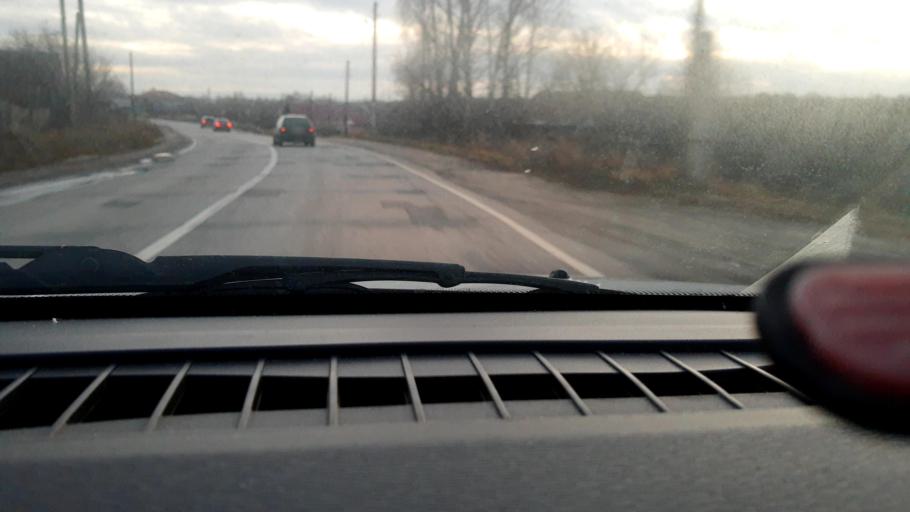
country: RU
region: Nizjnij Novgorod
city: Krasnyye Baki
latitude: 57.0690
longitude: 45.1378
